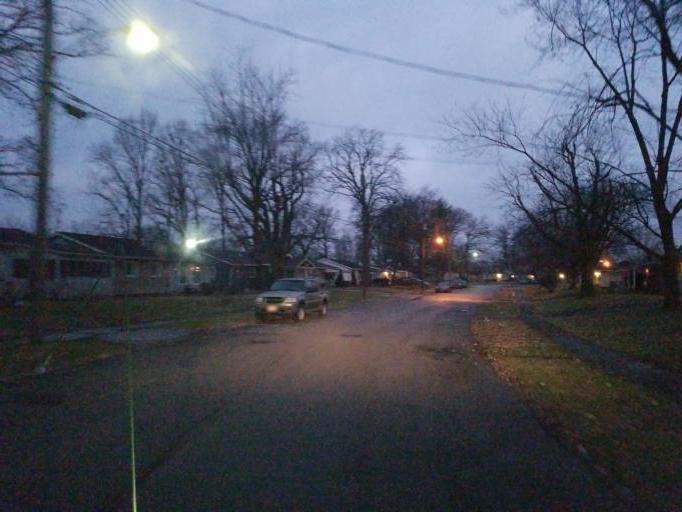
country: US
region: Ohio
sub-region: Marion County
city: Marion
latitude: 40.5736
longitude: -83.1377
